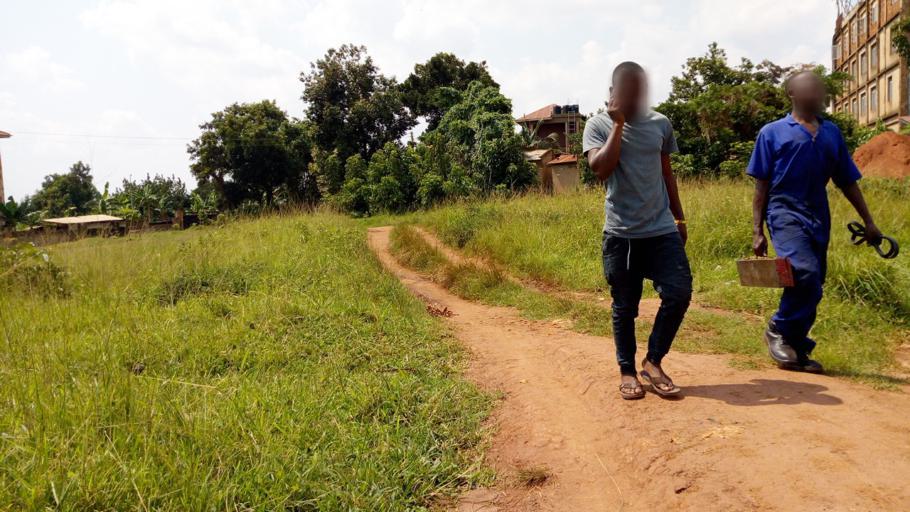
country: UG
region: Central Region
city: Kampala Central Division
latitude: 0.3434
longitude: 32.5641
